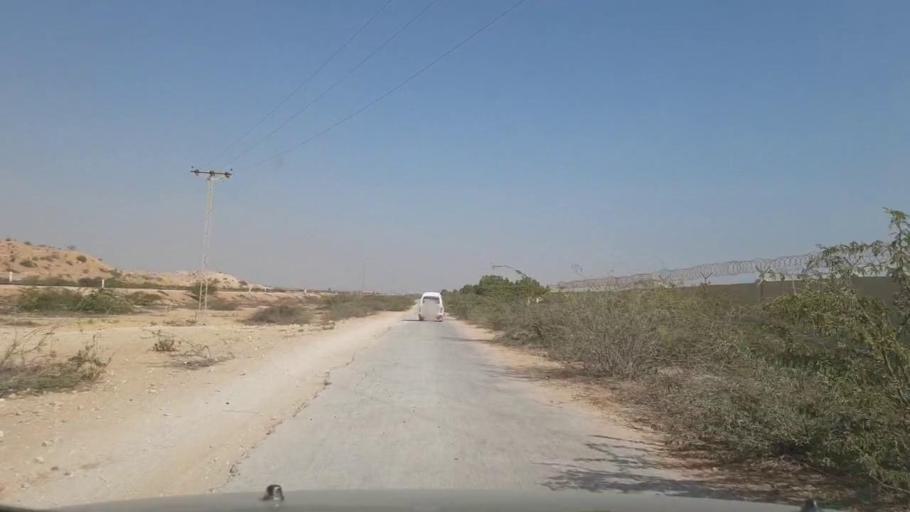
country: PK
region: Sindh
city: Thatta
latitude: 24.9897
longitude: 68.0021
